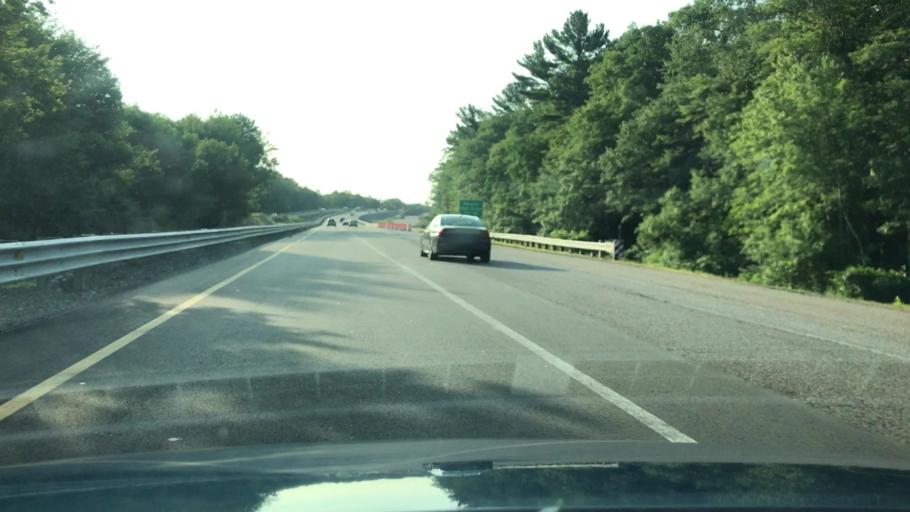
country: US
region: Massachusetts
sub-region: Plymouth County
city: Rockland
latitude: 42.1568
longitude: -70.8635
